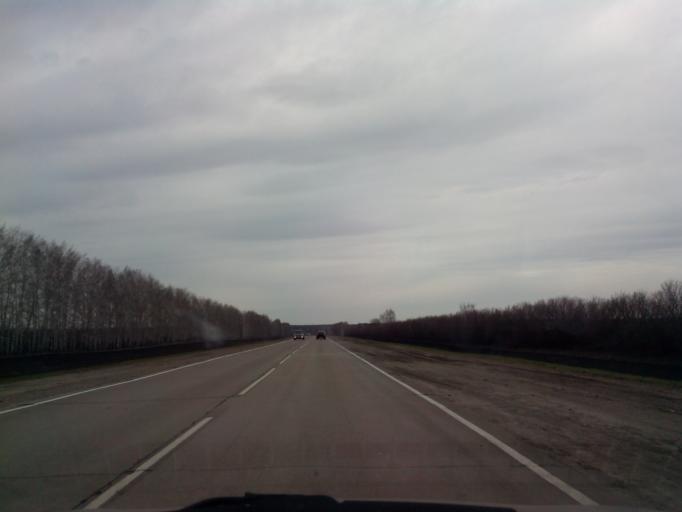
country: RU
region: Tambov
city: Znamenka
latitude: 52.5065
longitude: 41.3642
